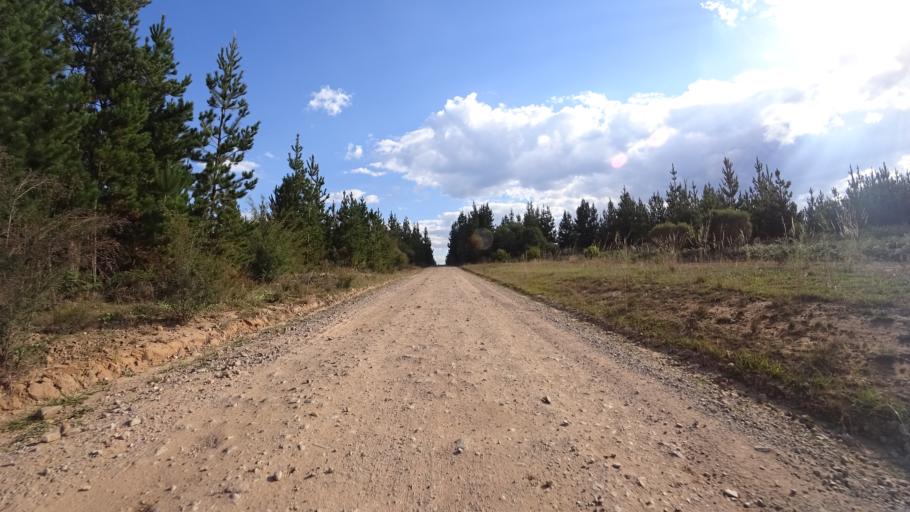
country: AU
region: New South Wales
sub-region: Lithgow
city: Lithgow
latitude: -33.3604
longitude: 150.2493
